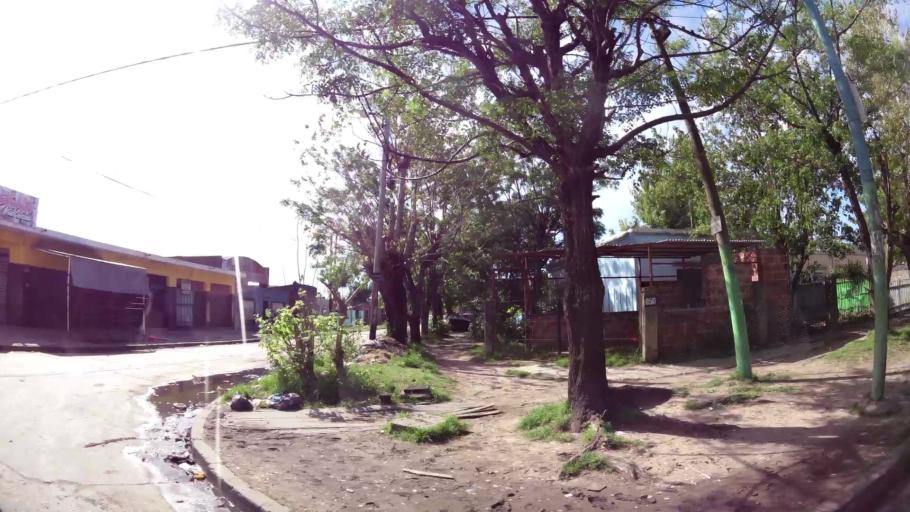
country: AR
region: Buenos Aires
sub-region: Partido de Quilmes
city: Quilmes
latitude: -34.7730
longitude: -58.2901
